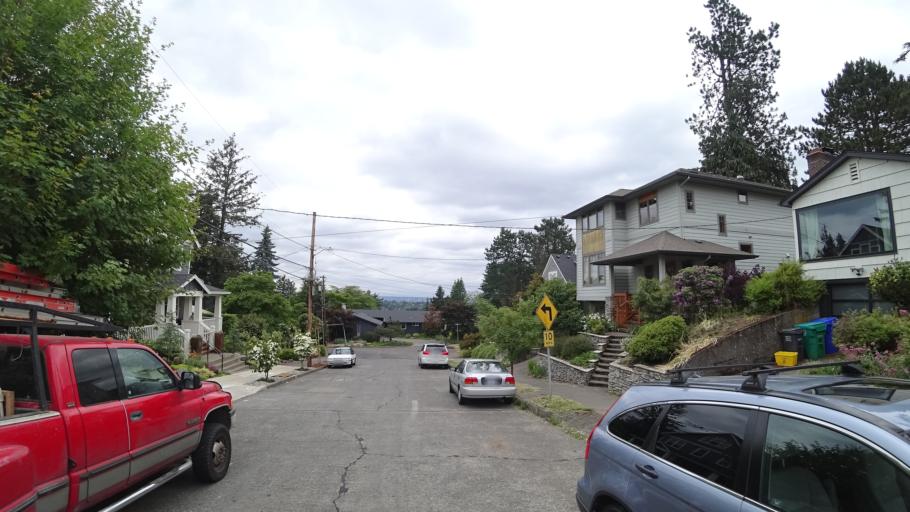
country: US
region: Oregon
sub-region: Multnomah County
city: Lents
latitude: 45.5198
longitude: -122.5942
